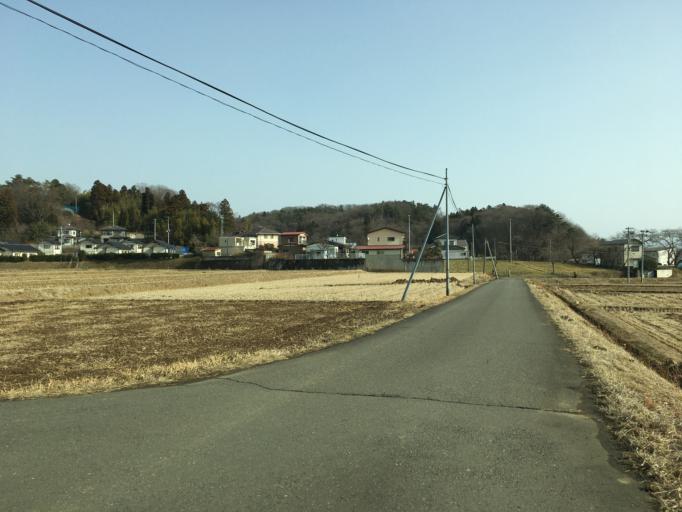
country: JP
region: Fukushima
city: Nihommatsu
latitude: 37.5650
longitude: 140.4025
